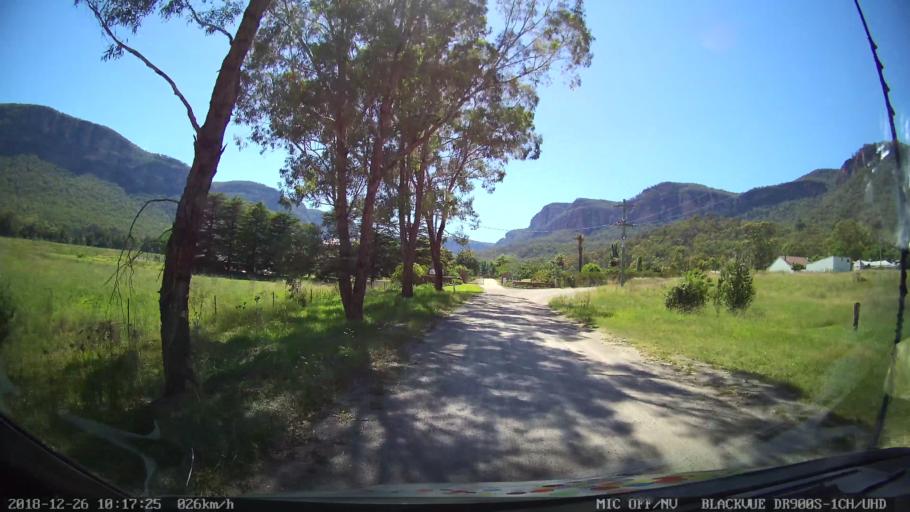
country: AU
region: New South Wales
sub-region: Lithgow
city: Portland
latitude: -33.1219
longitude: 150.2806
